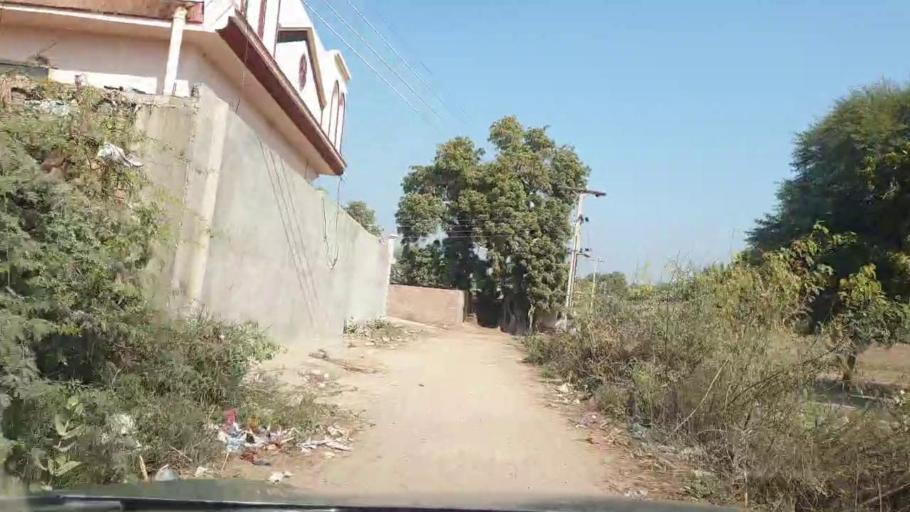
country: PK
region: Sindh
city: Tando Allahyar
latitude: 25.4671
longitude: 68.6369
